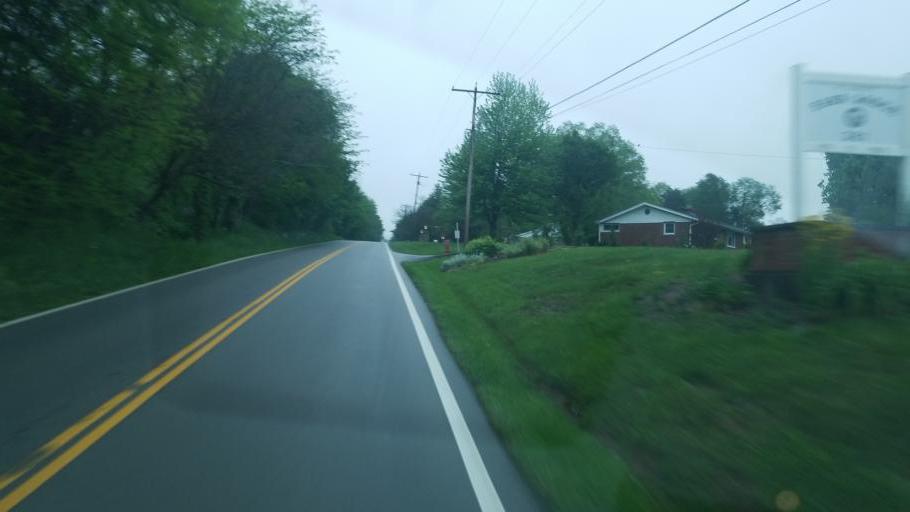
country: US
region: Ohio
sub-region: Highland County
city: Hillsboro
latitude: 39.1973
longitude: -83.6307
